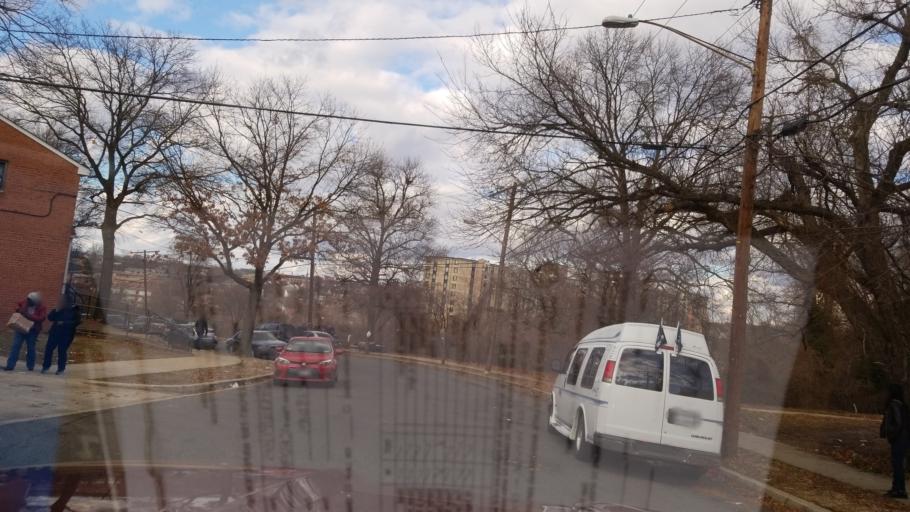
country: US
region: Maryland
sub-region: Prince George's County
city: Glassmanor
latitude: 38.8334
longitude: -76.9946
